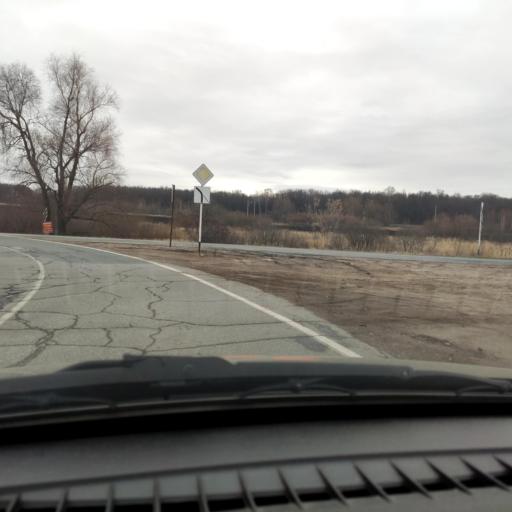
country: RU
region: Samara
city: Zhigulevsk
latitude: 53.3406
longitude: 49.4457
